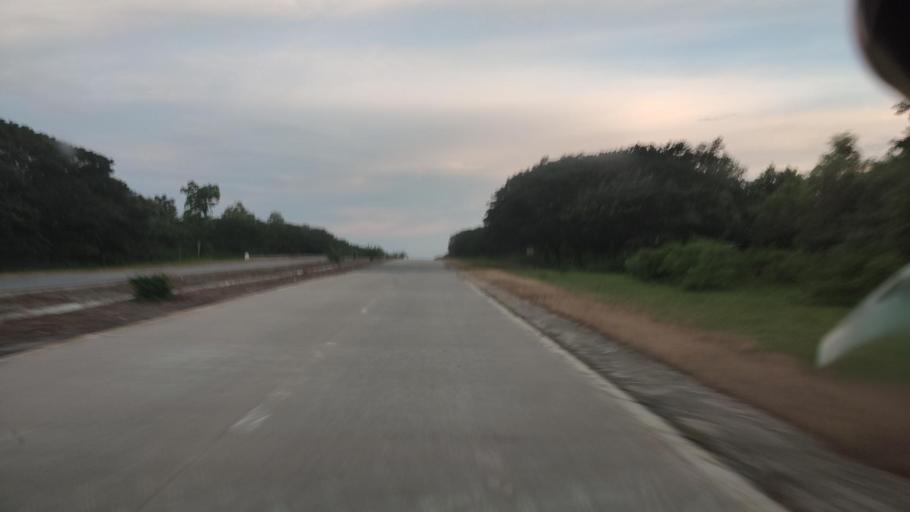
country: MM
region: Mandalay
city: Yamethin
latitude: 20.2551
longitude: 95.8931
